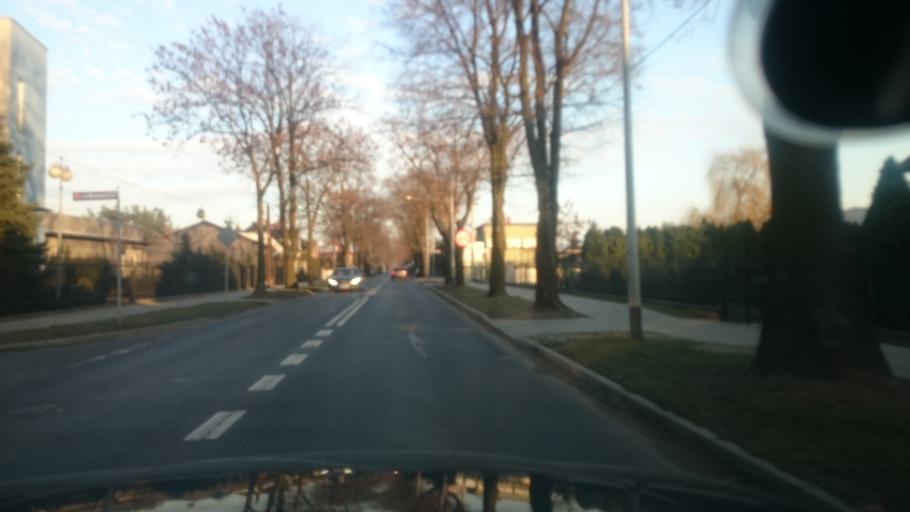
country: PL
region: Greater Poland Voivodeship
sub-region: Powiat ostrowski
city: Ostrow Wielkopolski
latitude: 51.6491
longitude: 17.8406
